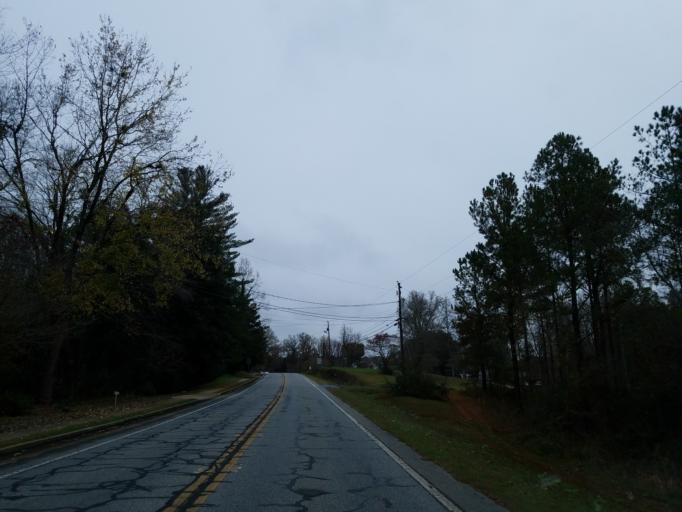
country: US
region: Georgia
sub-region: Cherokee County
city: Canton
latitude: 34.3086
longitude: -84.5550
